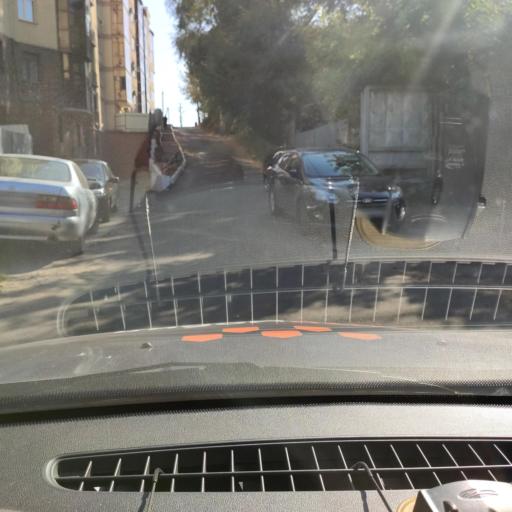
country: RU
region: Voronezj
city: Voronezh
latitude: 51.6600
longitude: 39.2105
